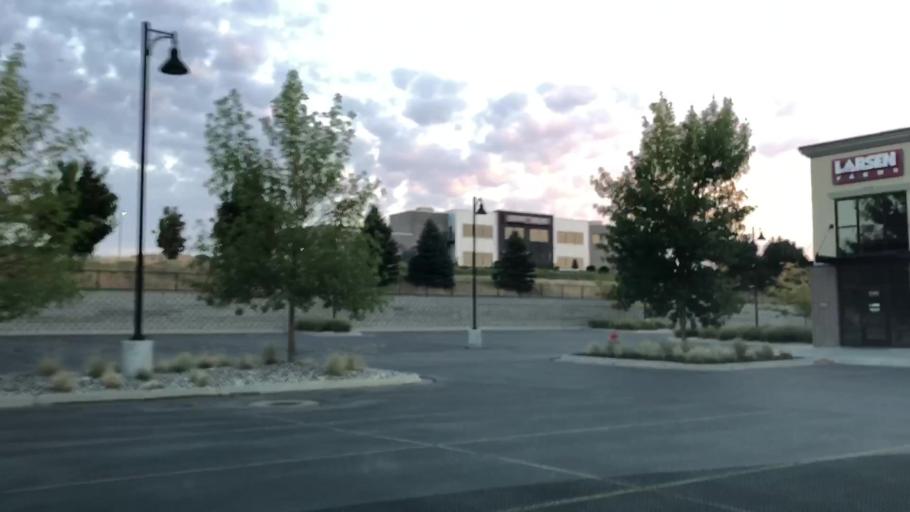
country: US
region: Idaho
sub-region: Bonneville County
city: Idaho Falls
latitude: 43.4846
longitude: -112.0536
